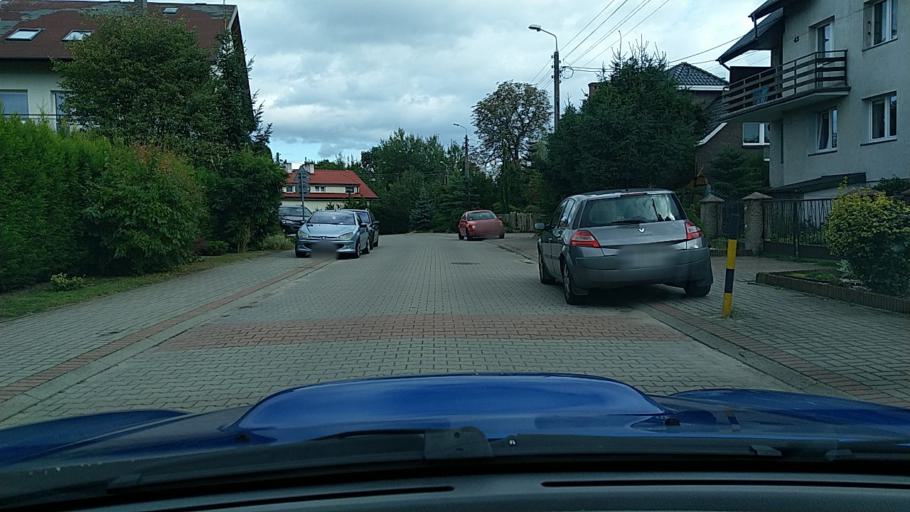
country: PL
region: Warmian-Masurian Voivodeship
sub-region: Olsztyn
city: Kortowo
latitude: 53.7657
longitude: 20.4193
